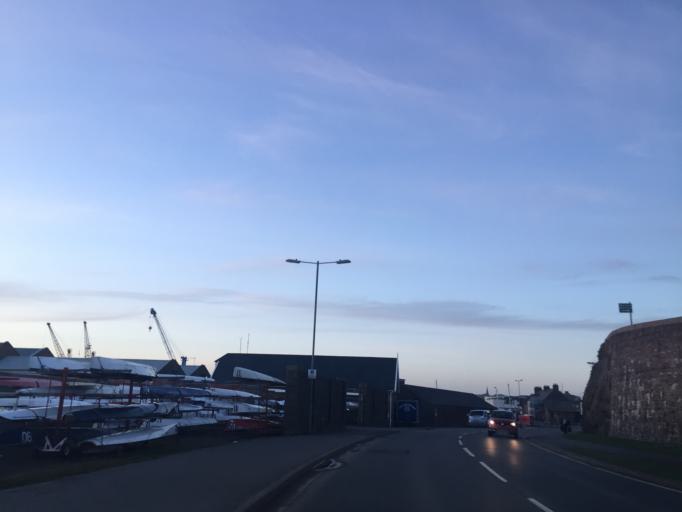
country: JE
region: St Helier
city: Saint Helier
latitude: 49.1763
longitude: -2.1108
